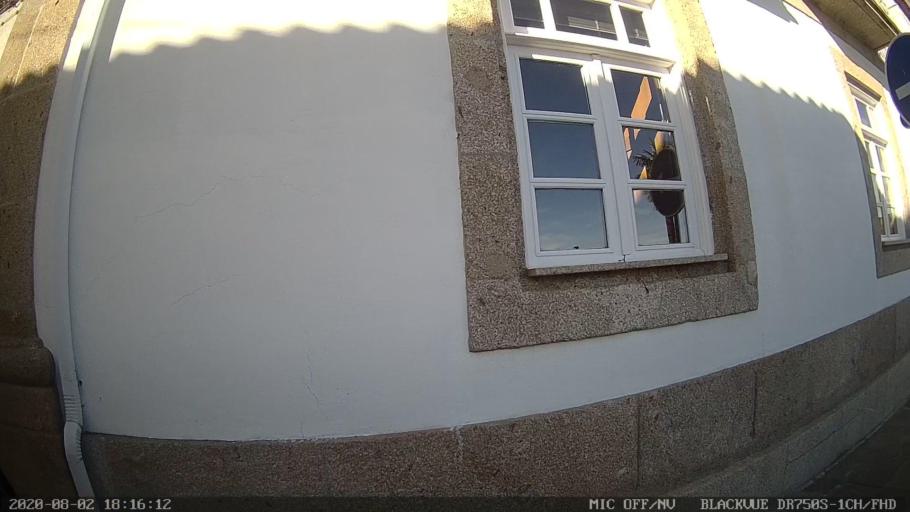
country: PT
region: Vila Real
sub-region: Murca
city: Murca
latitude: 41.4084
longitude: -7.4540
